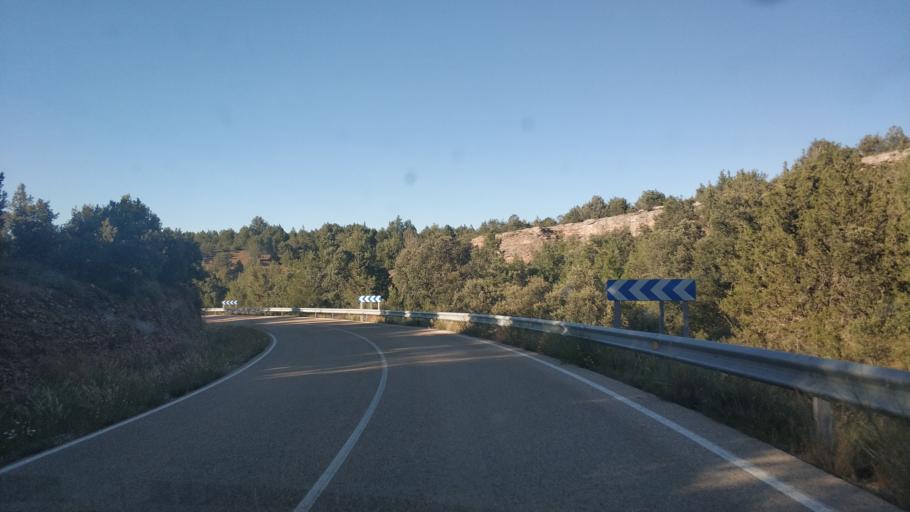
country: ES
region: Castille and Leon
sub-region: Provincia de Soria
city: Montejo de Tiermes
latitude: 41.4243
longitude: -3.2021
